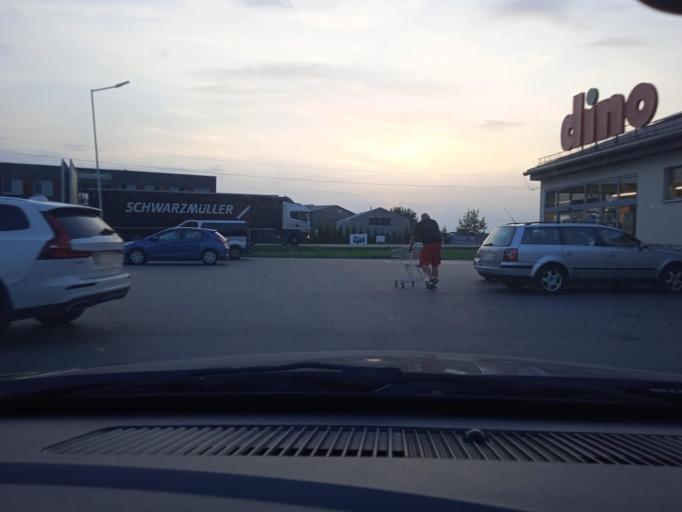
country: PL
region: Masovian Voivodeship
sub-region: Powiat nowodworski
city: Pomiechowek
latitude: 52.4674
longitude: 20.7230
